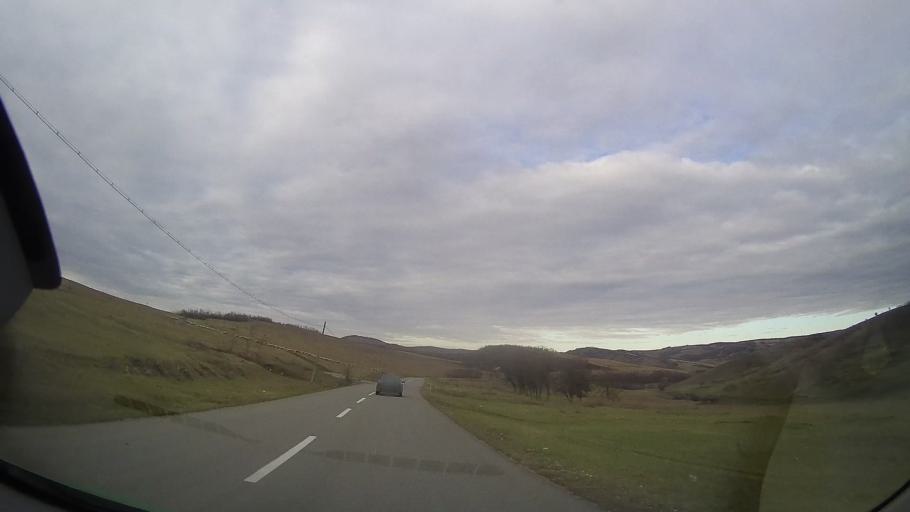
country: RO
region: Bistrita-Nasaud
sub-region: Comuna Milas
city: Milas
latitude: 46.8267
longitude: 24.4518
